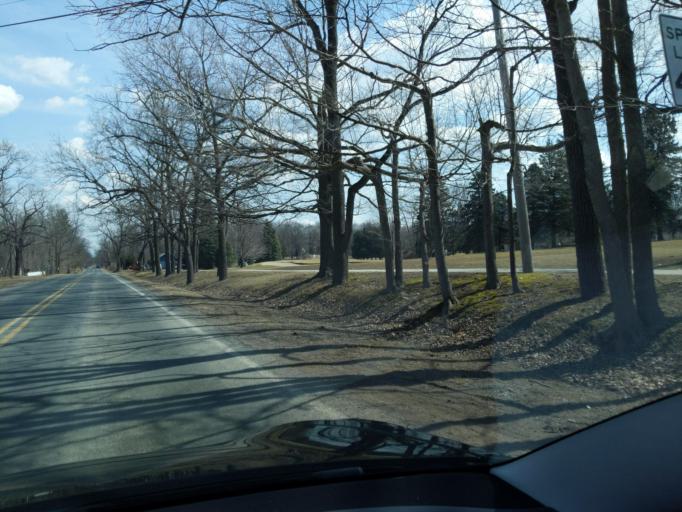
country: US
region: Michigan
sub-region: Washtenaw County
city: Chelsea
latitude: 42.3859
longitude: -84.0069
